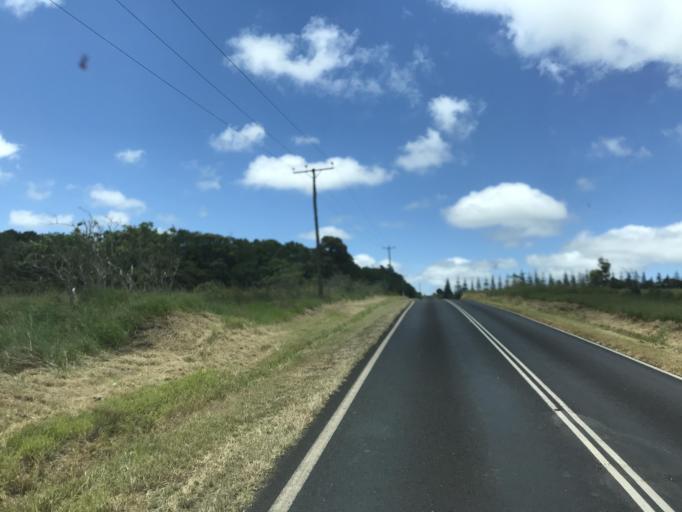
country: AU
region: Queensland
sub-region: Tablelands
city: Ravenshoe
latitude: -17.5034
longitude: 145.4763
